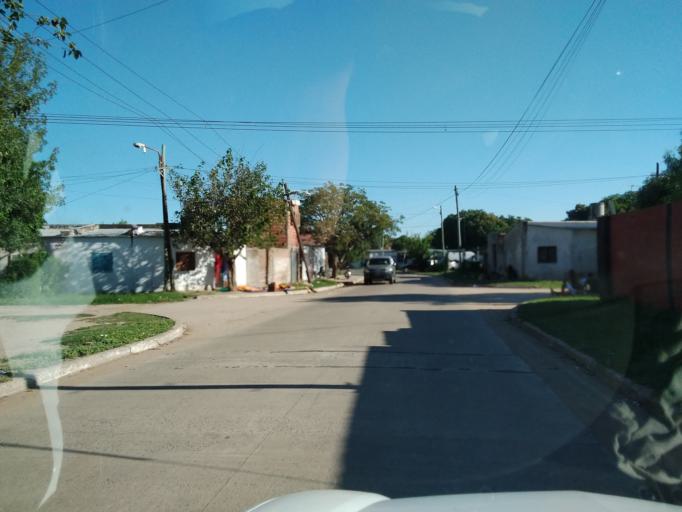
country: AR
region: Corrientes
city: Corrientes
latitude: -27.4741
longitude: -58.7921
